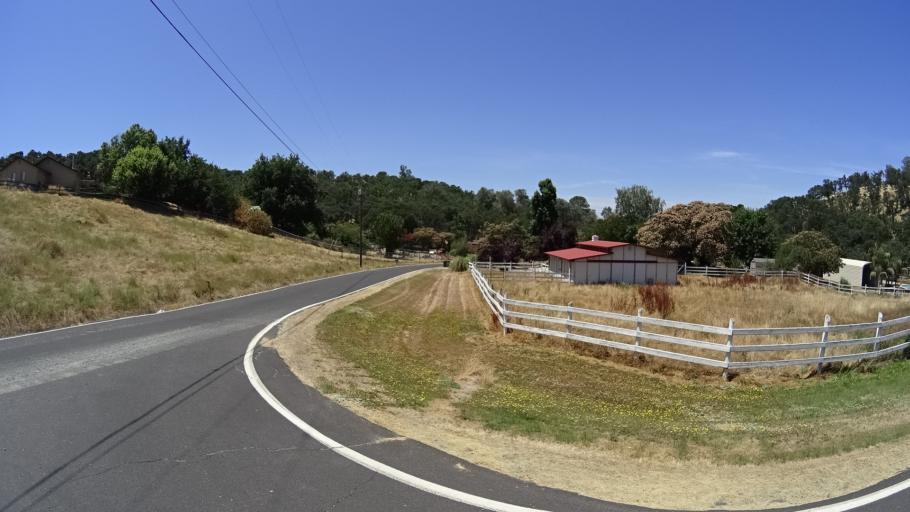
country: US
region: California
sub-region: Calaveras County
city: Rancho Calaveras
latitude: 38.1245
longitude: -120.8685
